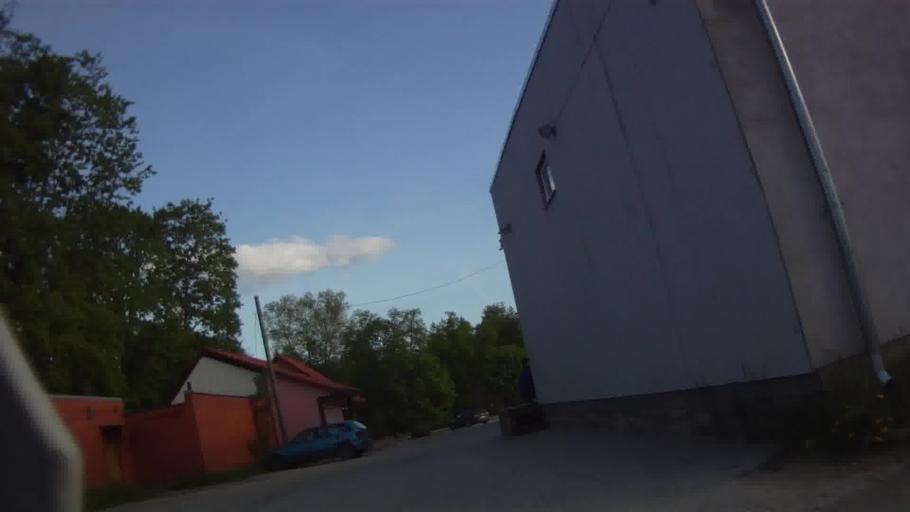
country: LV
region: Baldone
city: Baldone
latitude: 56.7430
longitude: 24.3981
